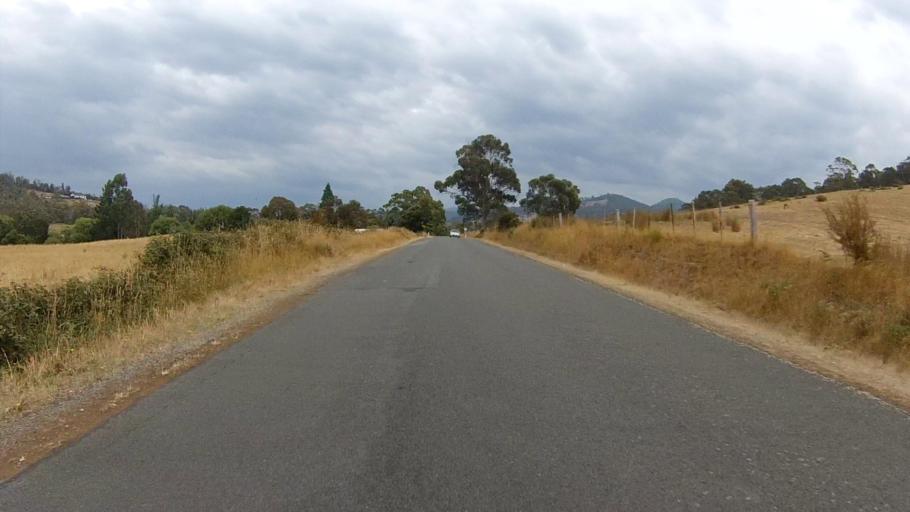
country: AU
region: Tasmania
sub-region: Huon Valley
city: Cygnet
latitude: -43.1829
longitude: 147.1111
